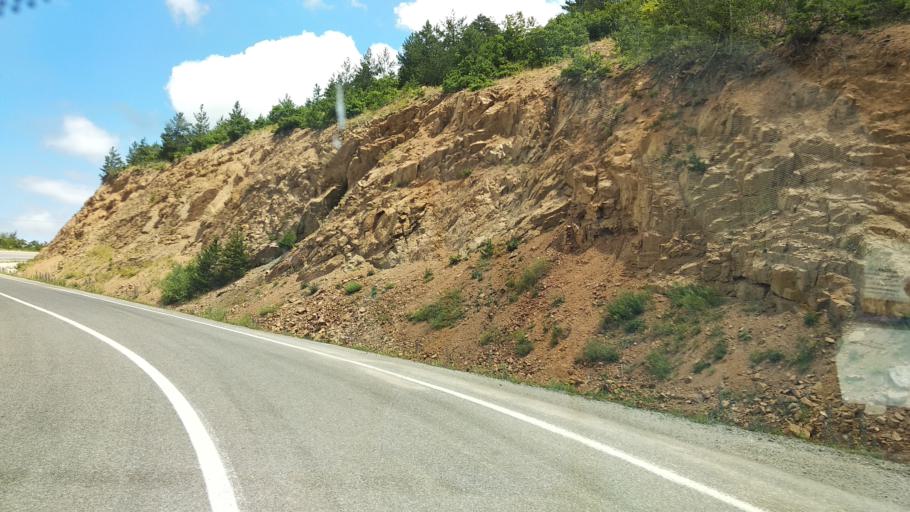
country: TR
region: Gumushane
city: Kose
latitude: 40.2982
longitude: 39.5639
